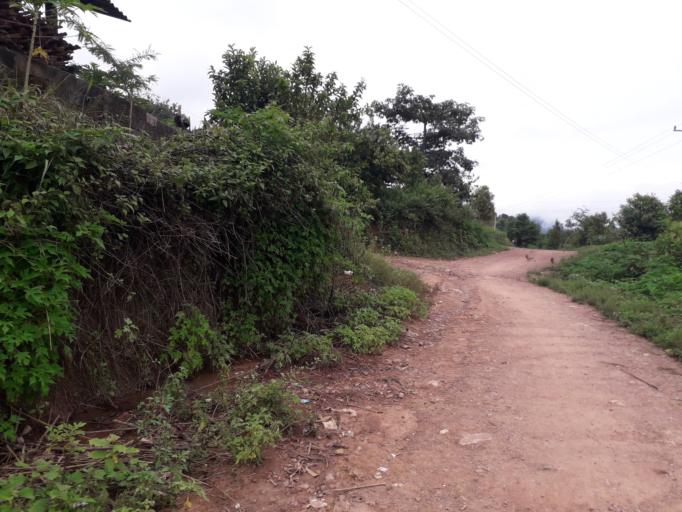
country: CN
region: Yunnan
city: Menglie
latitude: 22.2483
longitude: 101.6071
